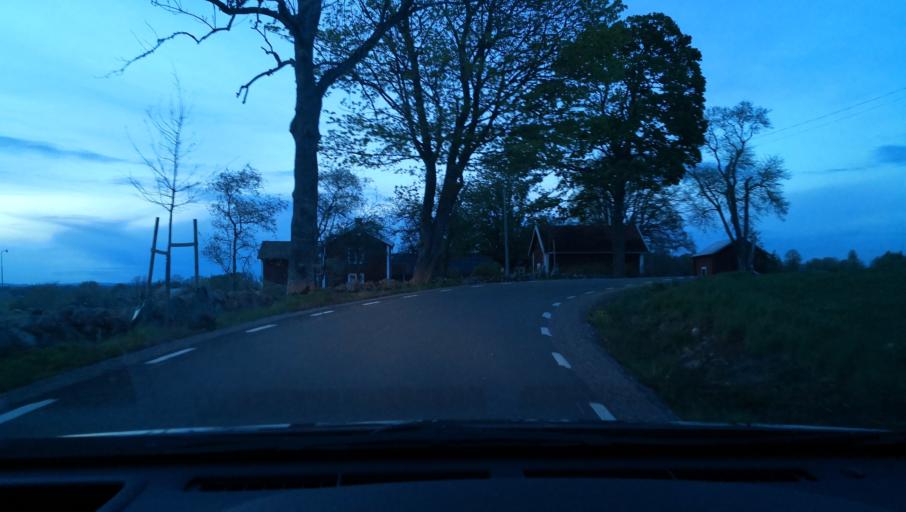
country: SE
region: OErebro
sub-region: Askersunds Kommun
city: Asbro
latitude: 59.0509
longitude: 14.9301
